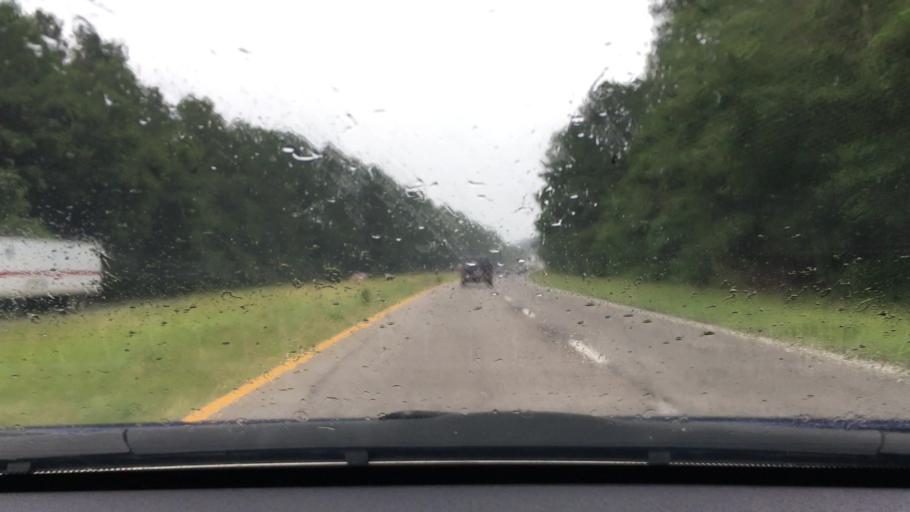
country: US
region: South Carolina
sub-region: Sumter County
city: Stateburg
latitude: 33.9524
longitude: -80.5633
